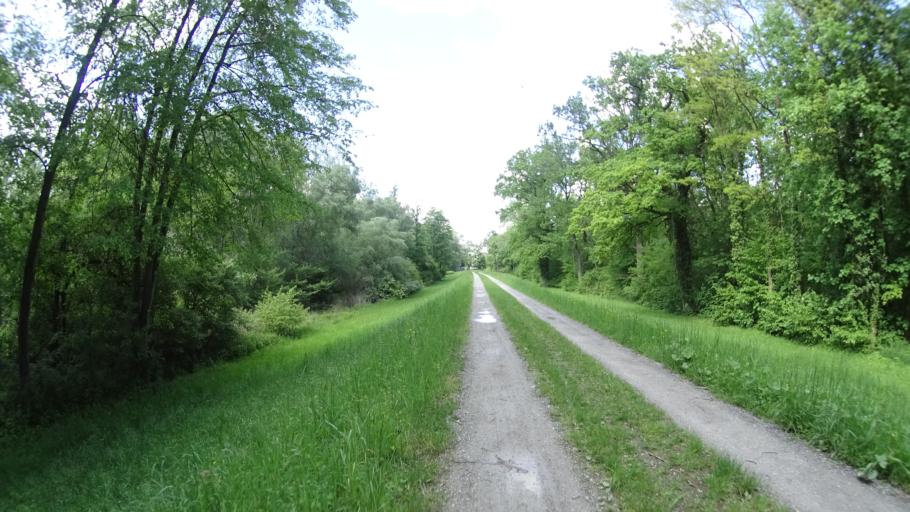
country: DE
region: Baden-Wuerttemberg
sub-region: Karlsruhe Region
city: Rheinstetten
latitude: 49.0092
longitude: 8.2997
